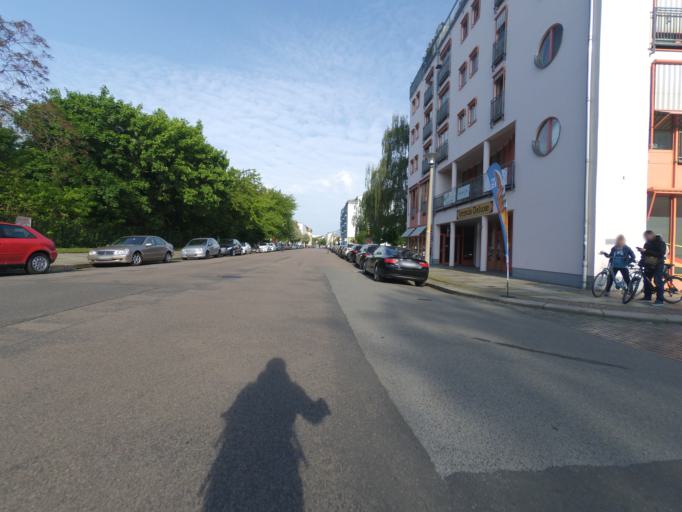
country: DE
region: Saxony
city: Dresden
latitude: 51.0517
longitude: 13.7639
